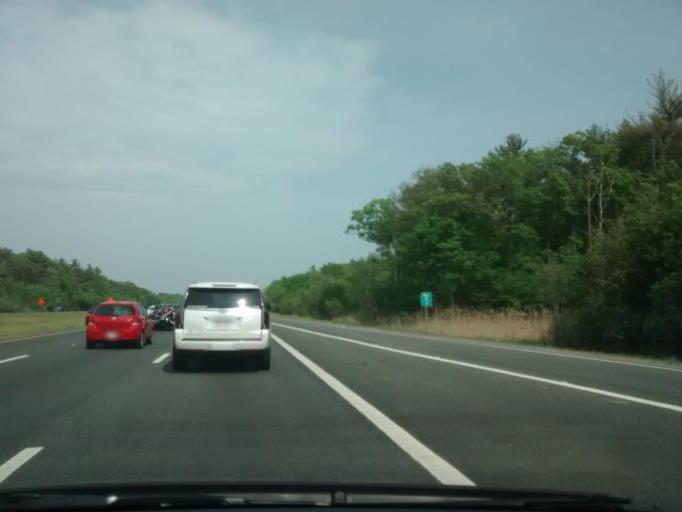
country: US
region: Massachusetts
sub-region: Bristol County
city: Raynham
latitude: 41.9585
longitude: -71.0644
